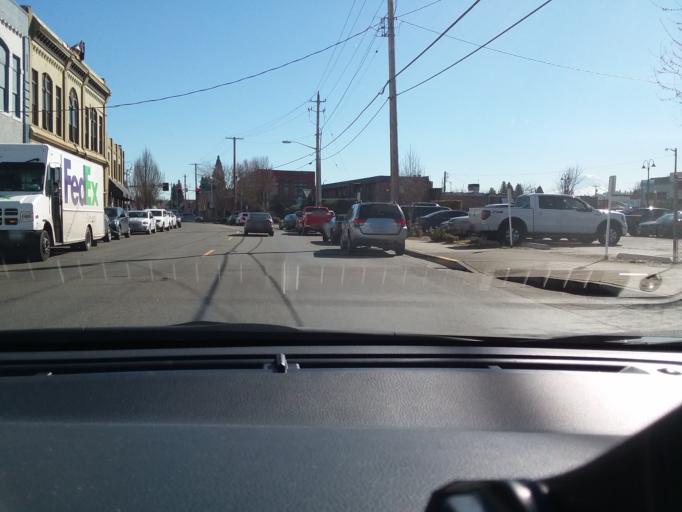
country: US
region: Washington
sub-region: Pierce County
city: Puyallup
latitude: 47.1931
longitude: -122.2952
